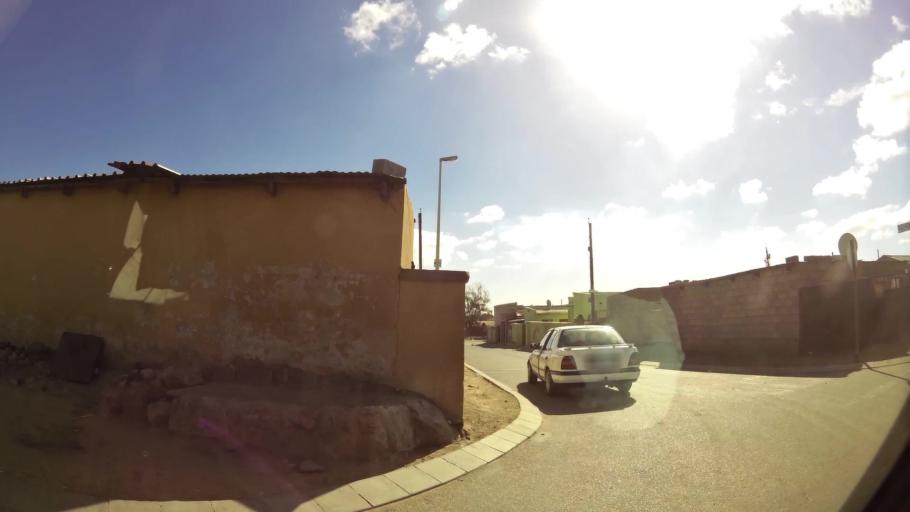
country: ZA
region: Gauteng
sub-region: City of Johannesburg Metropolitan Municipality
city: Modderfontein
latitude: -26.0425
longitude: 28.1795
